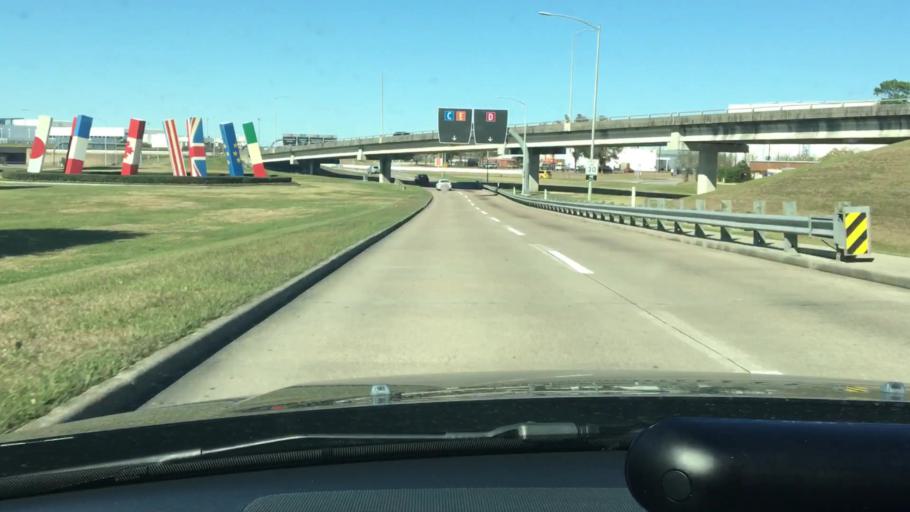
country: US
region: Texas
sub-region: Harris County
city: Humble
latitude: 29.9844
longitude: -95.3267
